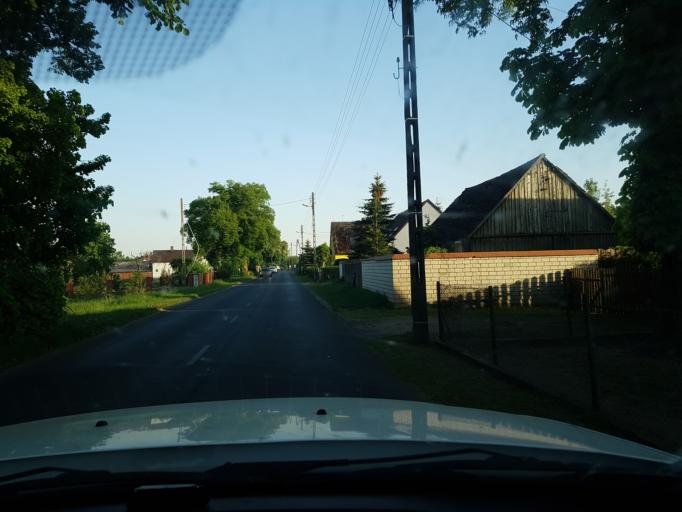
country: PL
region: West Pomeranian Voivodeship
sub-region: Powiat stargardzki
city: Kobylanka
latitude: 53.4258
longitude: 14.9018
